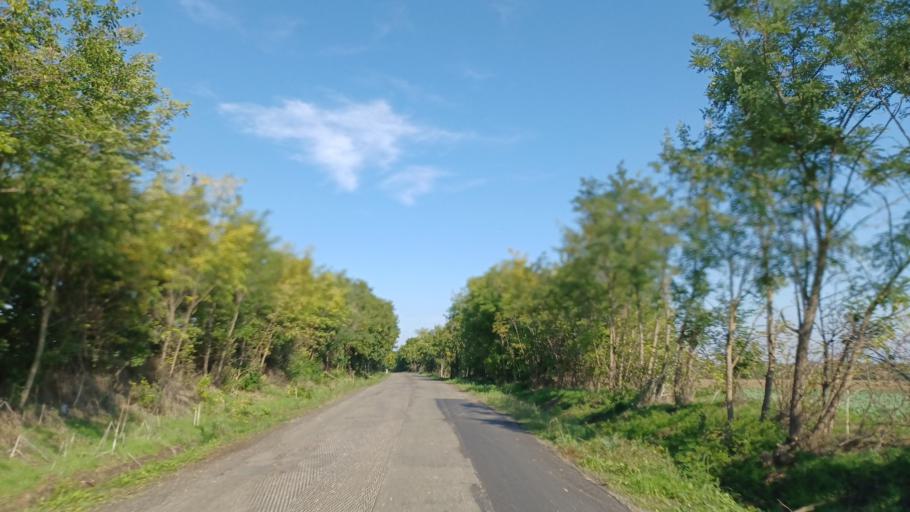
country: HU
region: Tolna
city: Nagydorog
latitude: 46.5899
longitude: 18.5964
